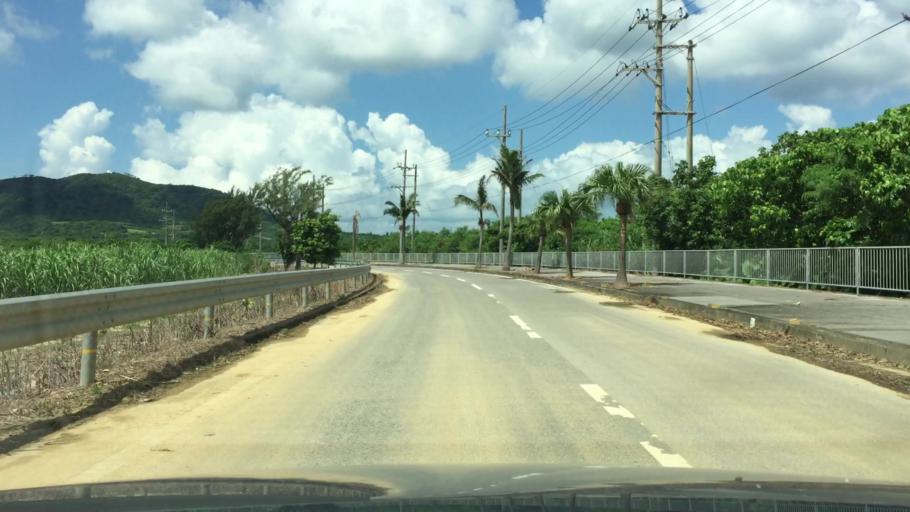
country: JP
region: Okinawa
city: Ishigaki
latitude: 24.3922
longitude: 124.1517
